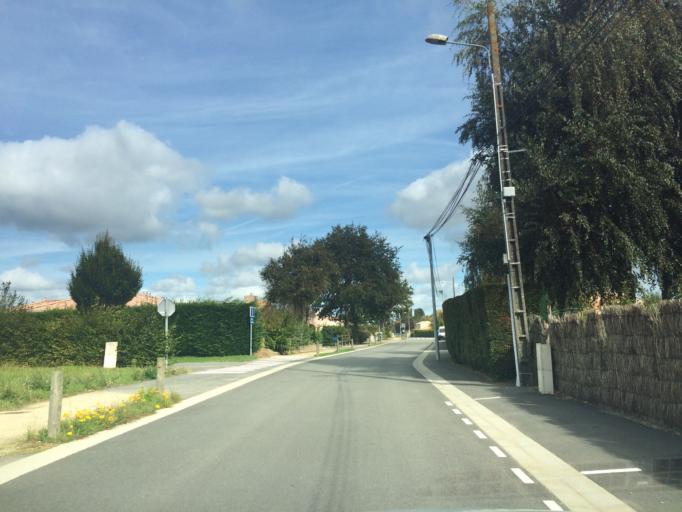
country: FR
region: Pays de la Loire
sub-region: Departement de la Loire-Atlantique
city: Chemere
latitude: 47.1135
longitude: -1.9168
